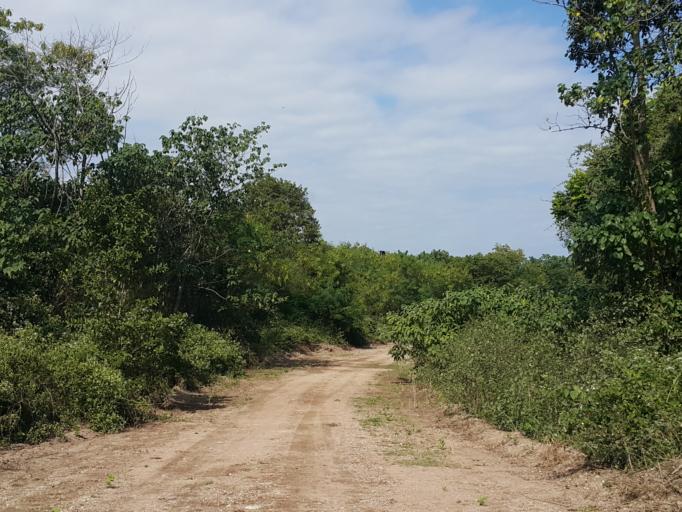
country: TH
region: Lampang
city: Mae Mo
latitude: 18.3279
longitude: 99.7647
